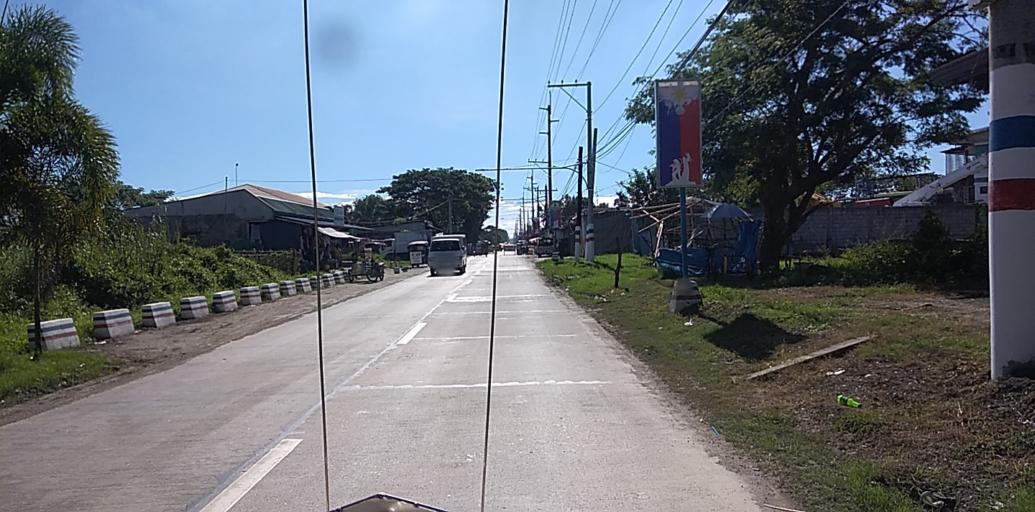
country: PH
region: Central Luzon
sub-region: Province of Pampanga
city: San Luis
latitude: 15.0532
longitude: 120.7798
